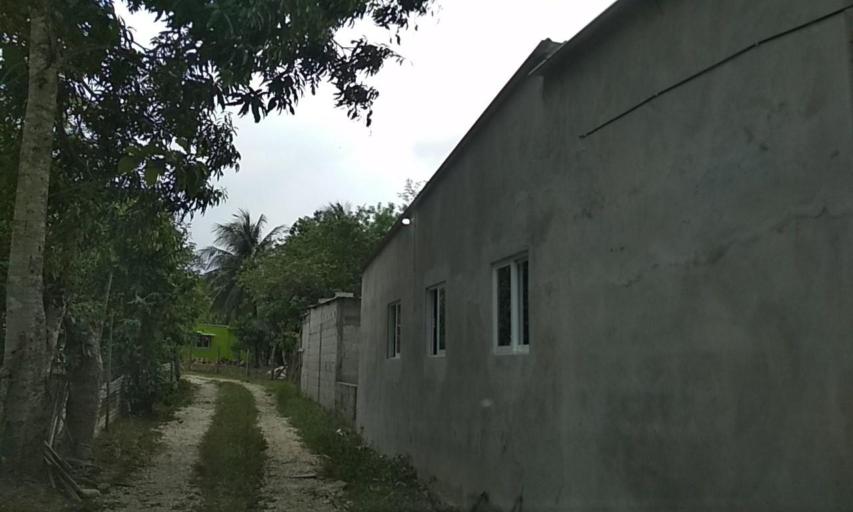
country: MX
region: Tabasco
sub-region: Huimanguillo
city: Francisco Rueda
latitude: 17.5689
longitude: -94.1090
